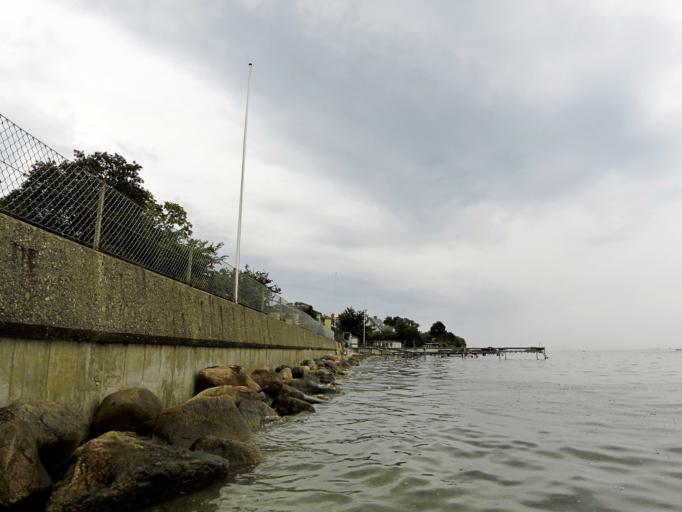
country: DK
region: Capital Region
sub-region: Gentofte Kommune
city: Charlottenlund
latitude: 55.7388
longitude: 12.5838
